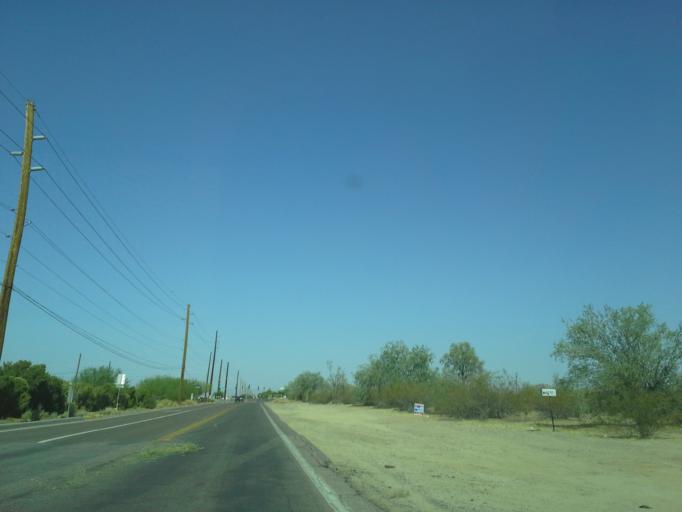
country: US
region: Arizona
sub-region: Maricopa County
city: Queen Creek
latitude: 33.2050
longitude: -111.6390
